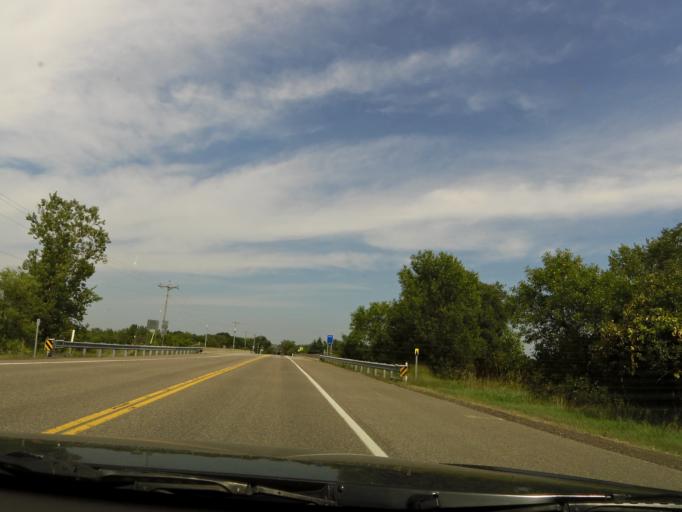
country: US
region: Minnesota
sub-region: Washington County
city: Lake Elmo
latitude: 44.9475
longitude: -92.8428
